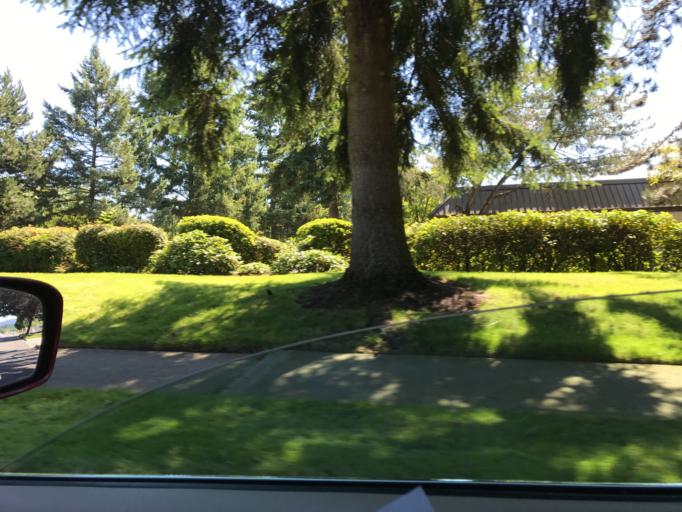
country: US
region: Washington
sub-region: King County
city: Redmond
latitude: 47.6382
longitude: -122.1430
